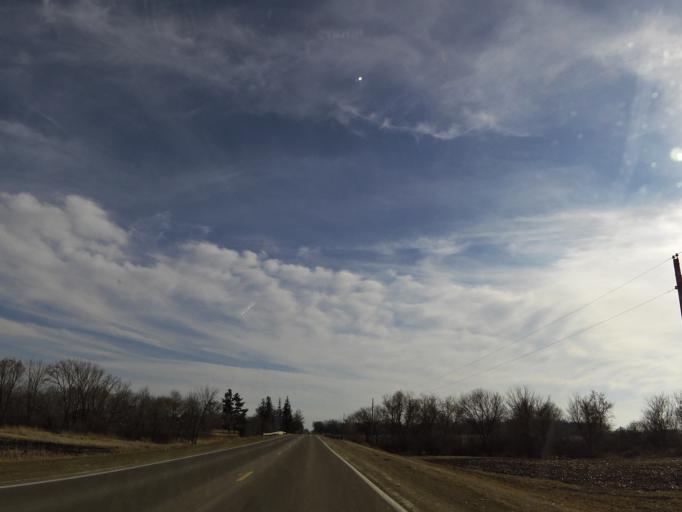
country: US
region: Minnesota
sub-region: Rice County
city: Northfield
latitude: 44.5235
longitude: -93.2003
